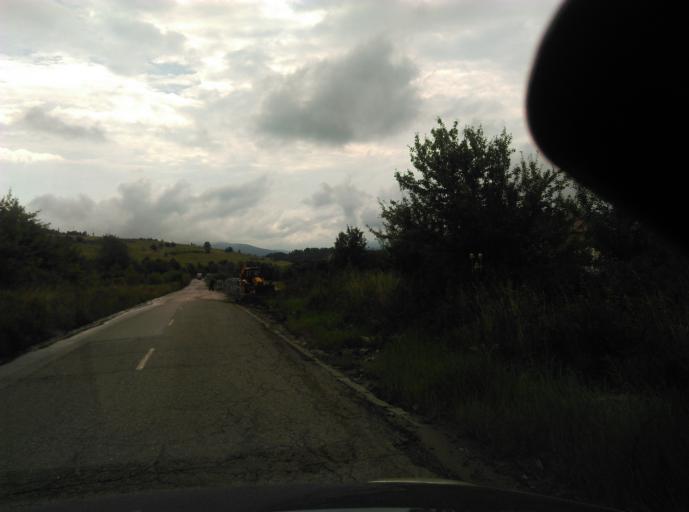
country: BG
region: Sofia-Capital
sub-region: Stolichna Obshtina
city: Sofia
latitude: 42.5896
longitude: 23.3755
